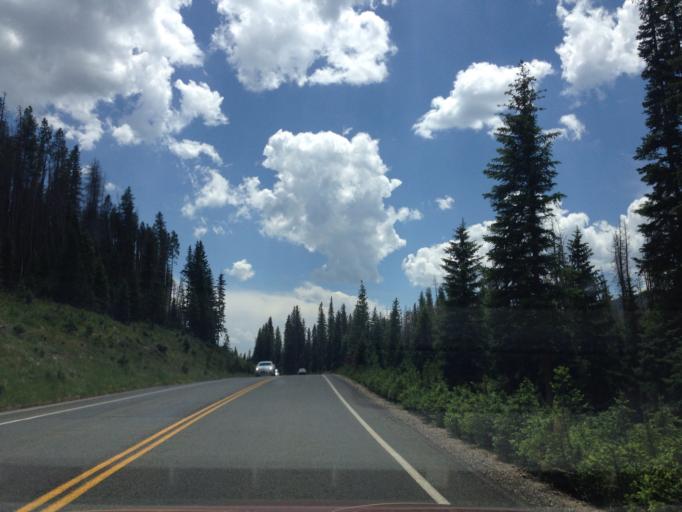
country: US
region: Colorado
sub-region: Grand County
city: Granby
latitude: 40.3476
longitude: -105.8575
